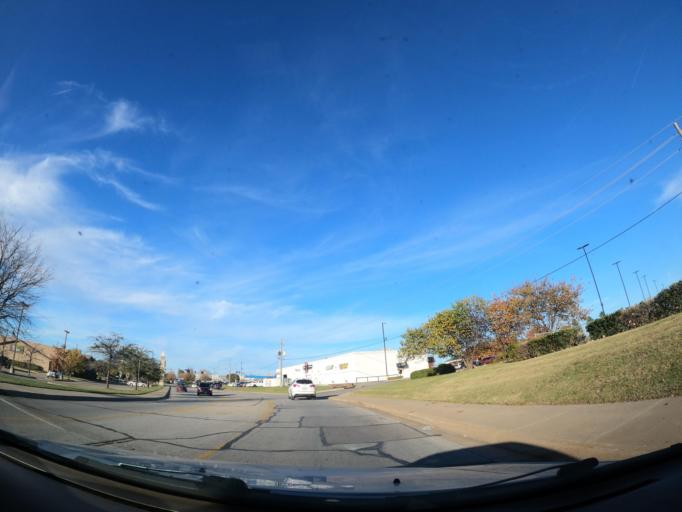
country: US
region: Oklahoma
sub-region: Tulsa County
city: Owasso
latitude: 36.2917
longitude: -95.8394
